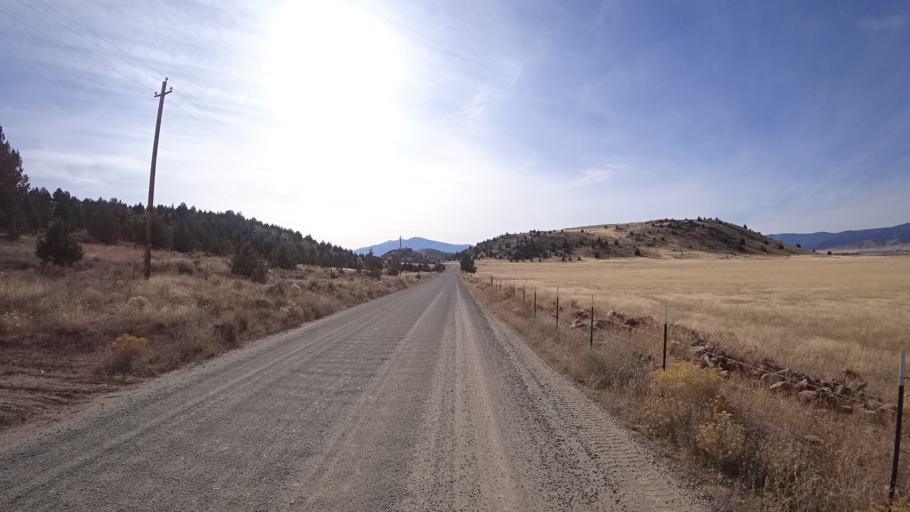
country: US
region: California
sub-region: Siskiyou County
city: Montague
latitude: 41.5722
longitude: -122.4658
